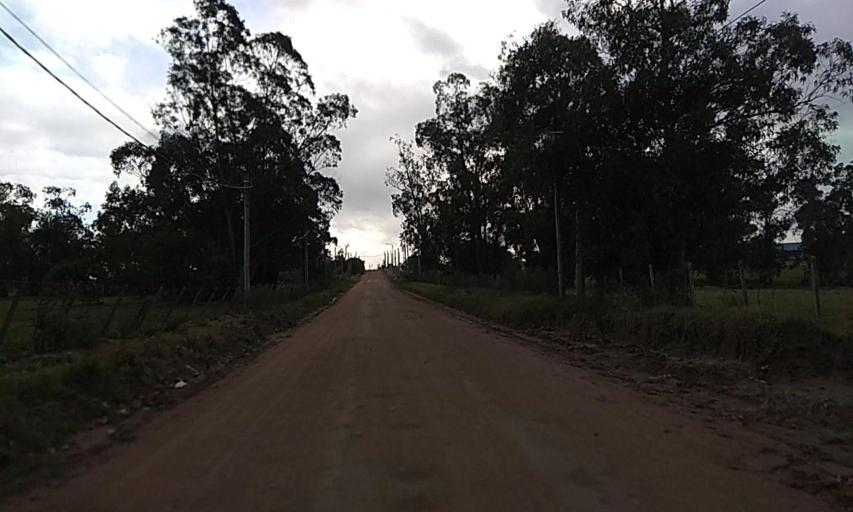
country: UY
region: Florida
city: Florida
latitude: -34.0788
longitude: -56.2018
